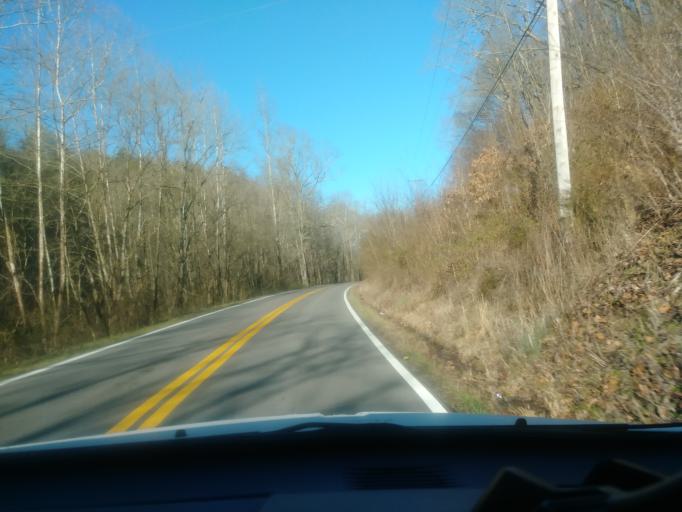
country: US
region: Tennessee
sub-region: Greene County
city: Mosheim
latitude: 36.1220
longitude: -83.0064
